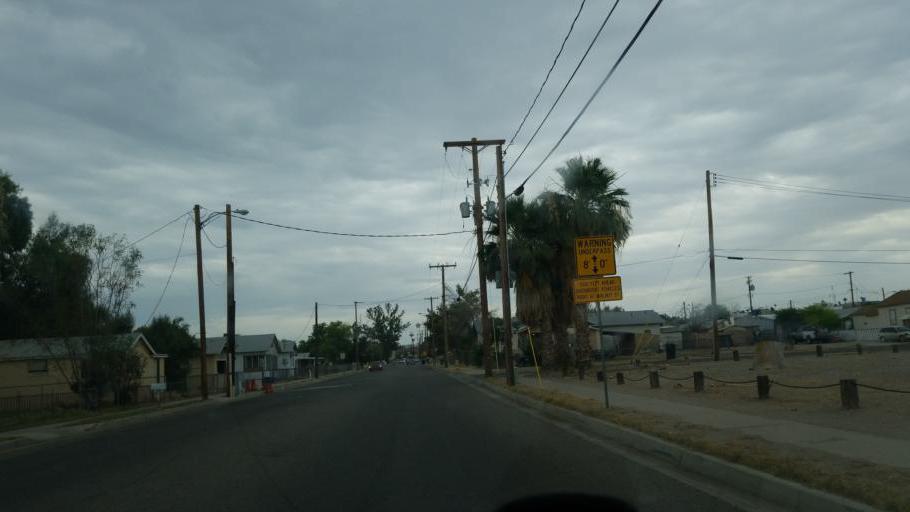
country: US
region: California
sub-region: San Bernardino County
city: Needles
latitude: 34.8480
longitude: -114.6105
